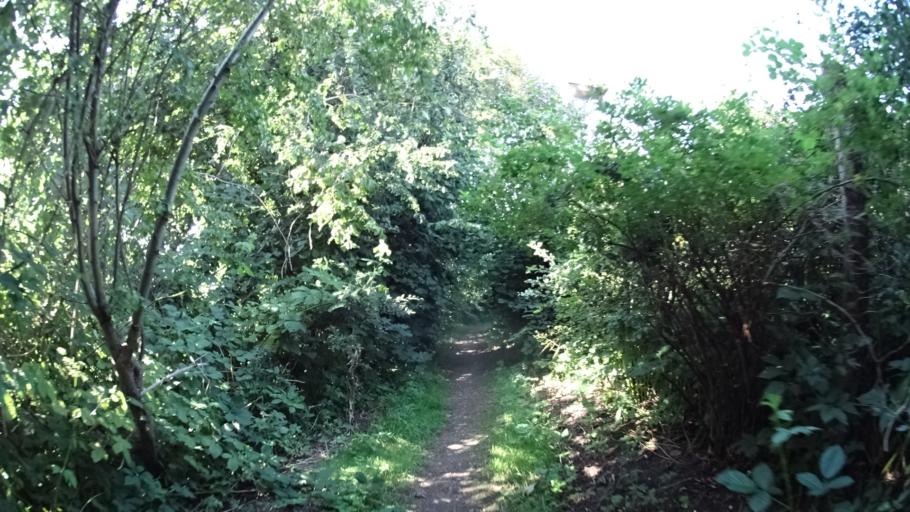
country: DK
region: Central Jutland
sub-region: Arhus Kommune
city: Stavtrup
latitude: 56.1567
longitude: 10.1064
